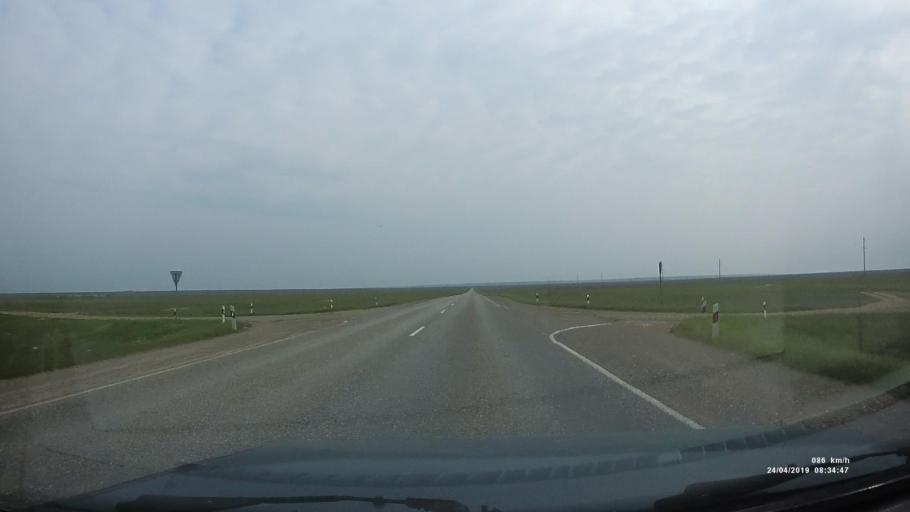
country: RU
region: Kalmykiya
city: Arshan'
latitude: 46.1927
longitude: 43.9095
